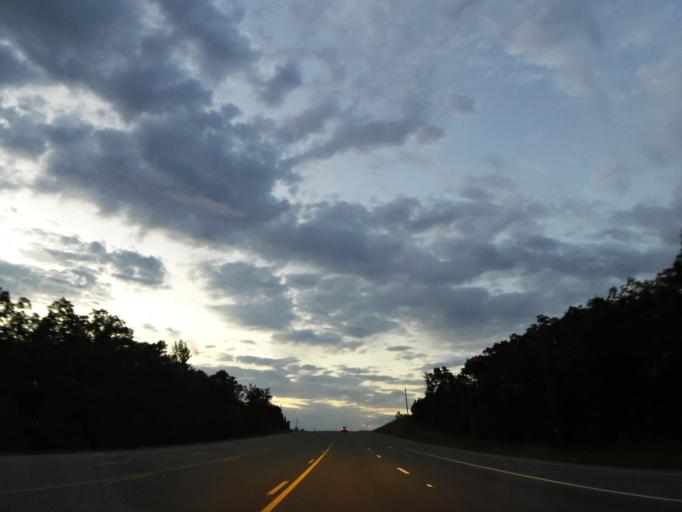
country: US
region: Alabama
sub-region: Marion County
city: Winfield
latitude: 33.9804
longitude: -87.7753
